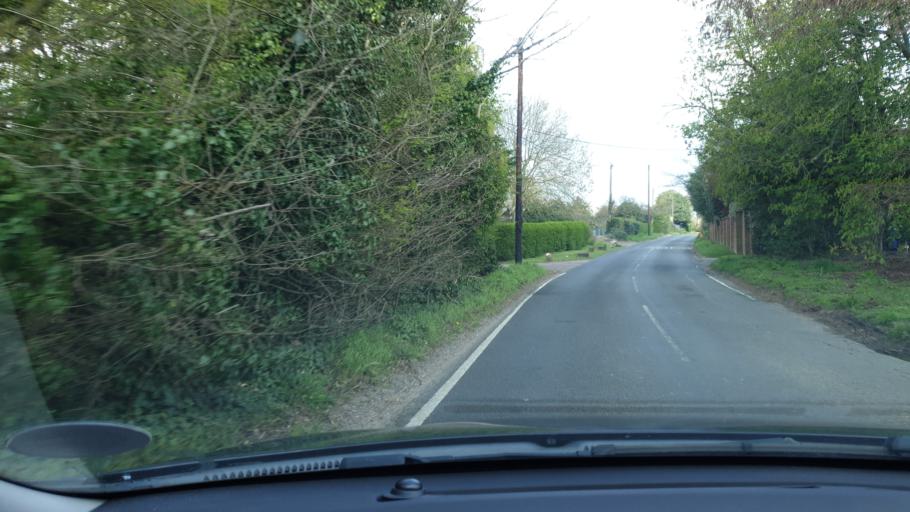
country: GB
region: England
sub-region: Essex
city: Great Bentley
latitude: 51.8640
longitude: 1.1004
